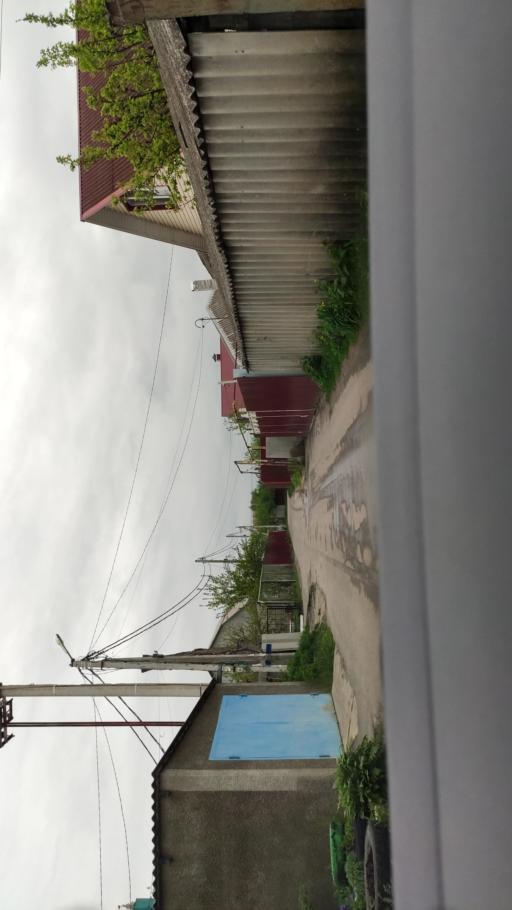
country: RU
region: Voronezj
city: Novaya Usman'
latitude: 51.6414
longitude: 39.4184
